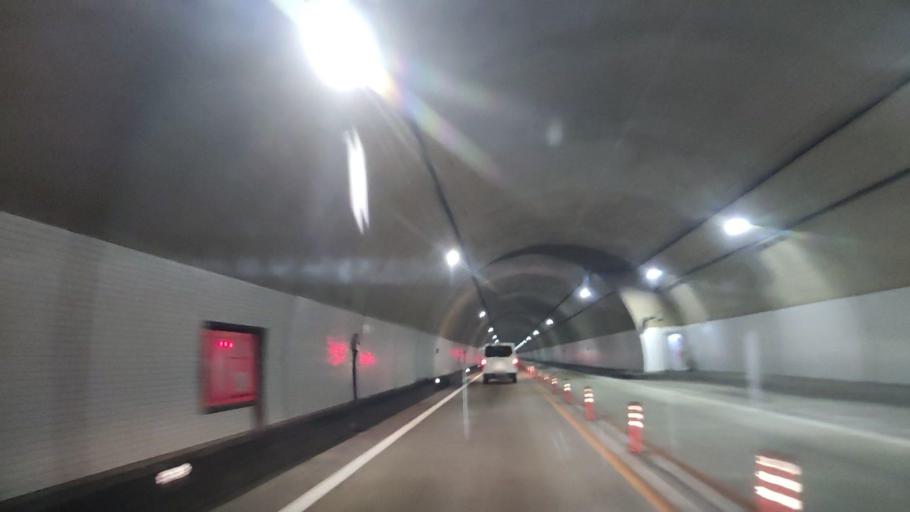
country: JP
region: Akita
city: Odate
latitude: 40.3407
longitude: 140.6339
